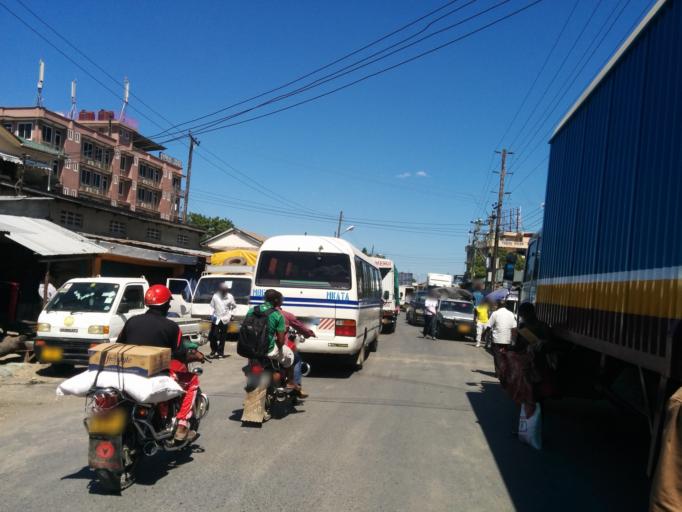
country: TZ
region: Dar es Salaam
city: Magomeni
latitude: -6.7978
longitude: 39.2334
